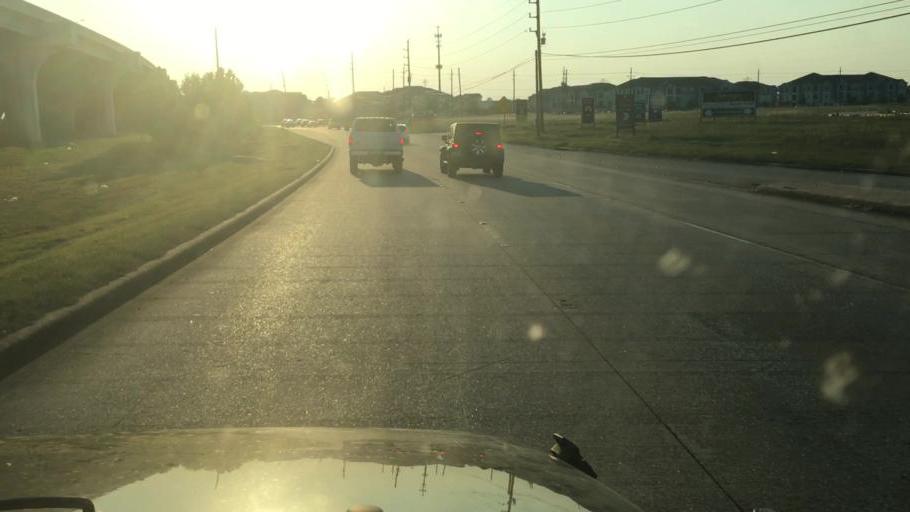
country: US
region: Texas
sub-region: Harris County
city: Atascocita
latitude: 29.9340
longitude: -95.2091
